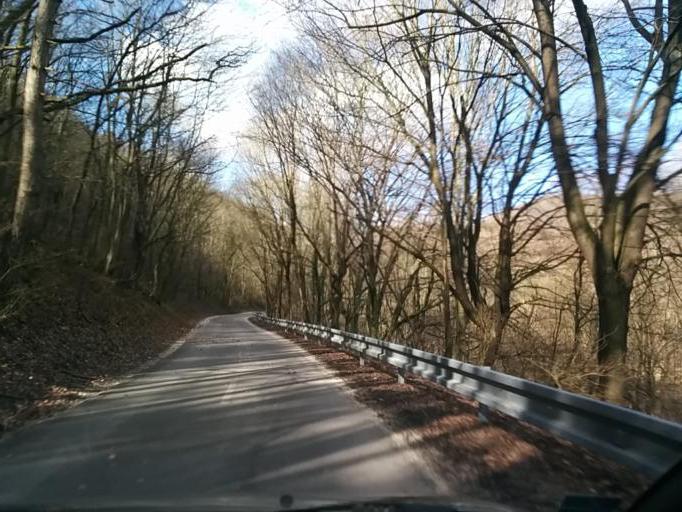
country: SK
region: Nitriansky
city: Cachtice
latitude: 48.7342
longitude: 17.7748
